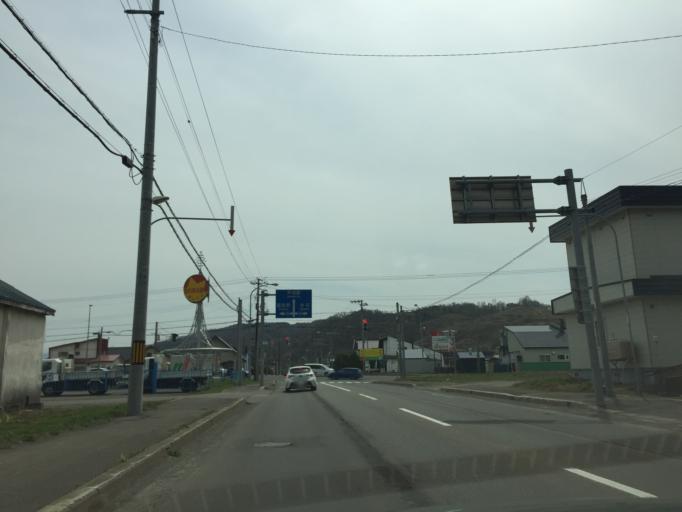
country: JP
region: Hokkaido
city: Ashibetsu
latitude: 43.5315
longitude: 142.1706
